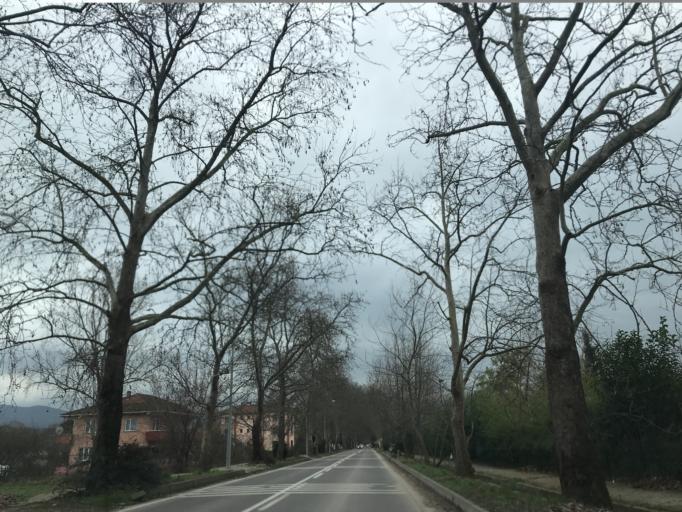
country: TR
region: Yalova
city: Kadikoy
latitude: 40.6369
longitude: 29.2256
